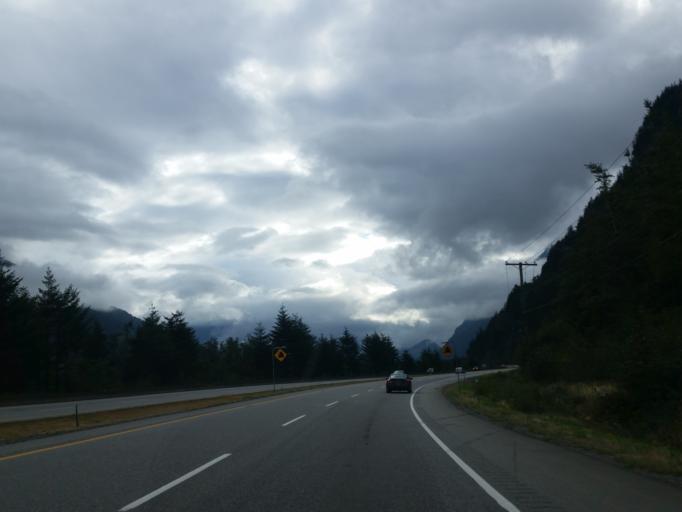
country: CA
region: British Columbia
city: Hope
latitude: 49.3641
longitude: -121.5473
